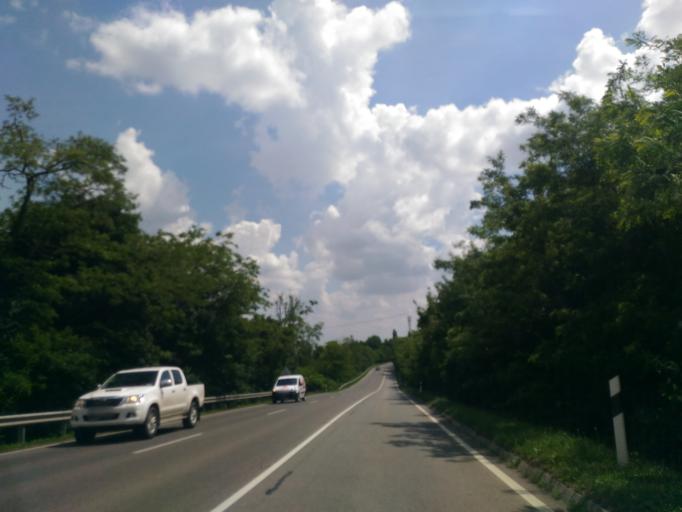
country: HU
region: Baranya
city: Pecs
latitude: 46.1248
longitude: 18.2595
